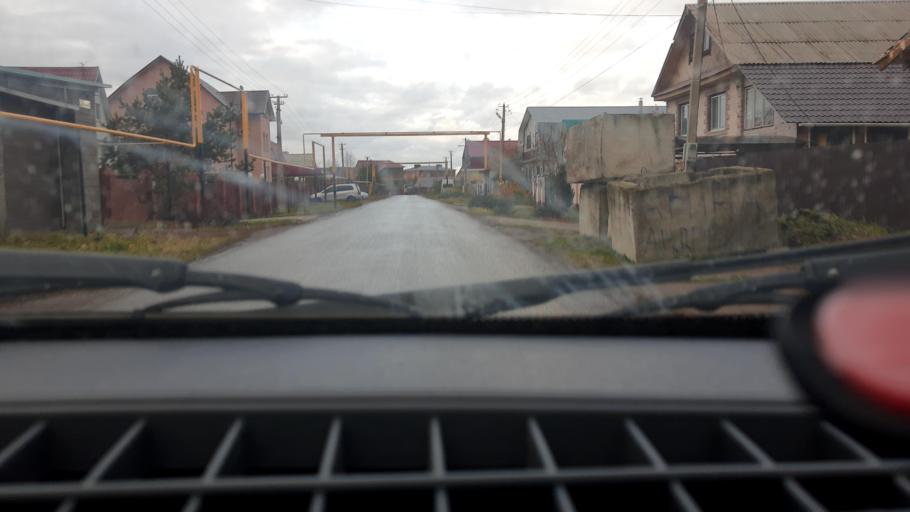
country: RU
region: Bashkortostan
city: Mikhaylovka
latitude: 54.8058
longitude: 55.9391
